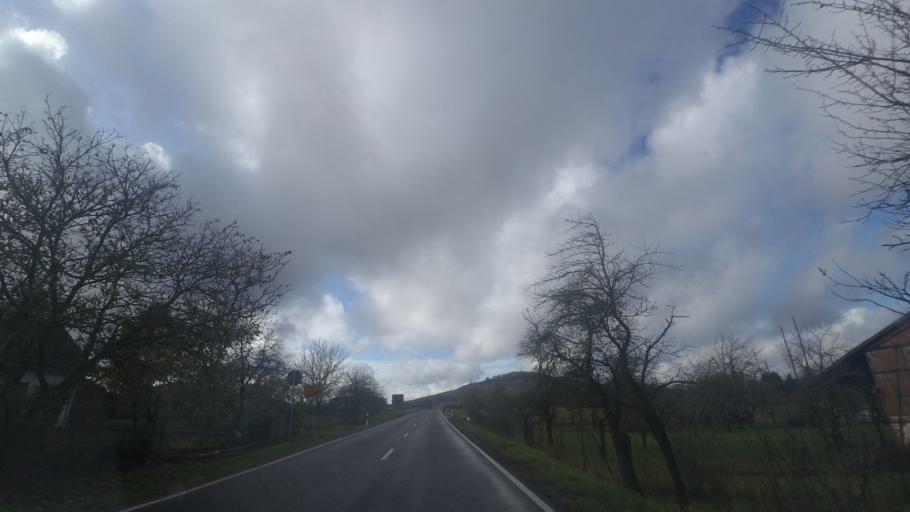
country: DE
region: Thuringia
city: Dingsleben
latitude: 50.4126
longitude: 10.6323
